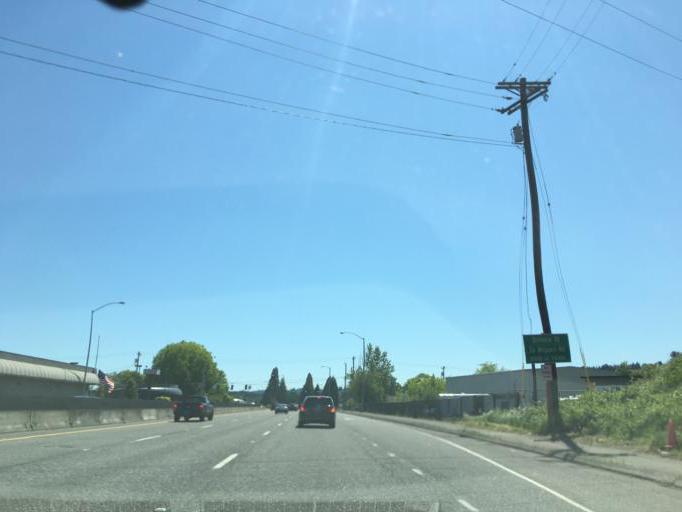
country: US
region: Oregon
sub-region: Clackamas County
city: Milwaukie
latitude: 45.4604
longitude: -122.6394
